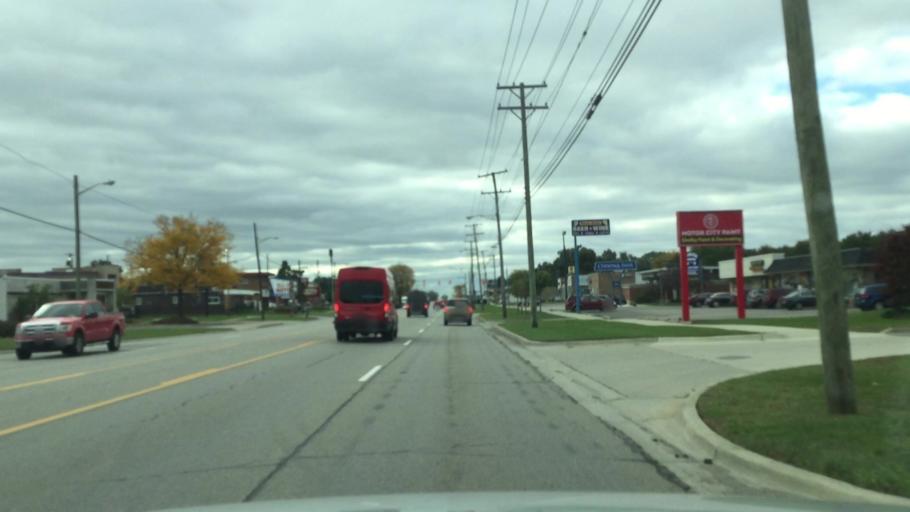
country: US
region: Michigan
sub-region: Macomb County
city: Utica
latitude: 42.6428
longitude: -83.0331
